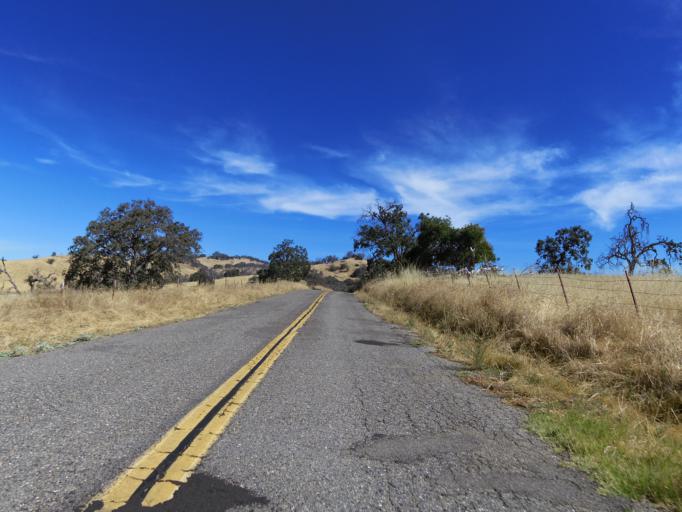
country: US
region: California
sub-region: Mariposa County
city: Mariposa
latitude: 37.3671
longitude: -119.9667
